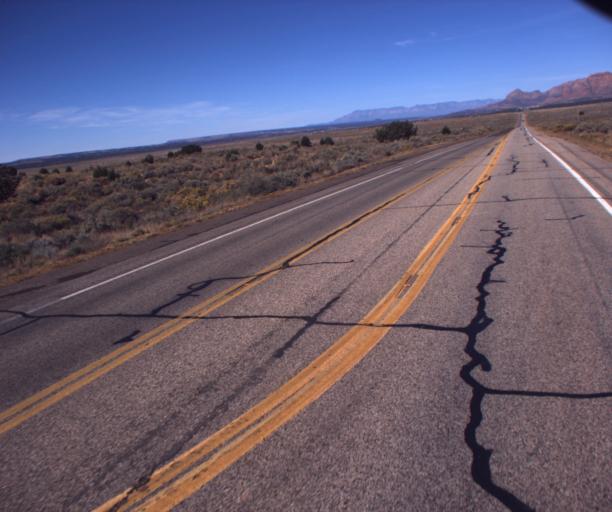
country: US
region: Arizona
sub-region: Mohave County
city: Colorado City
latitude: 36.9041
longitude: -112.9222
